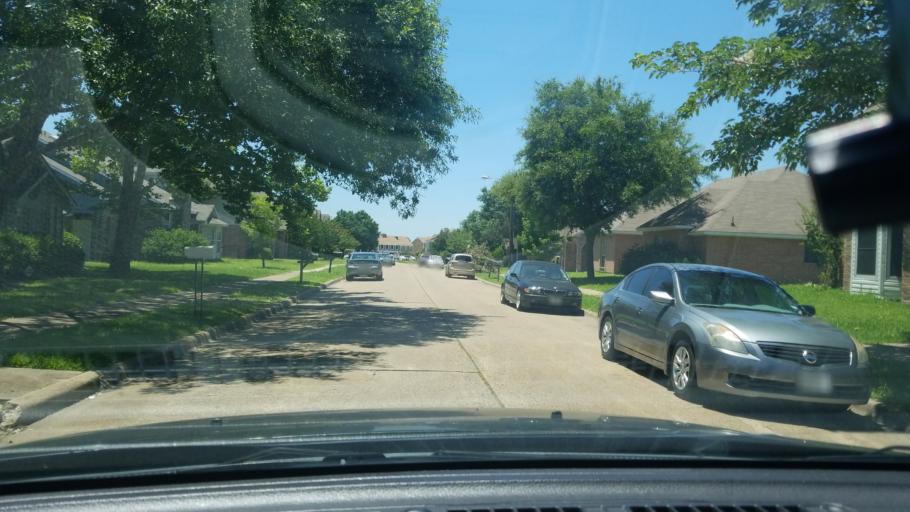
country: US
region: Texas
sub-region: Dallas County
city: Mesquite
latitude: 32.7722
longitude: -96.6063
